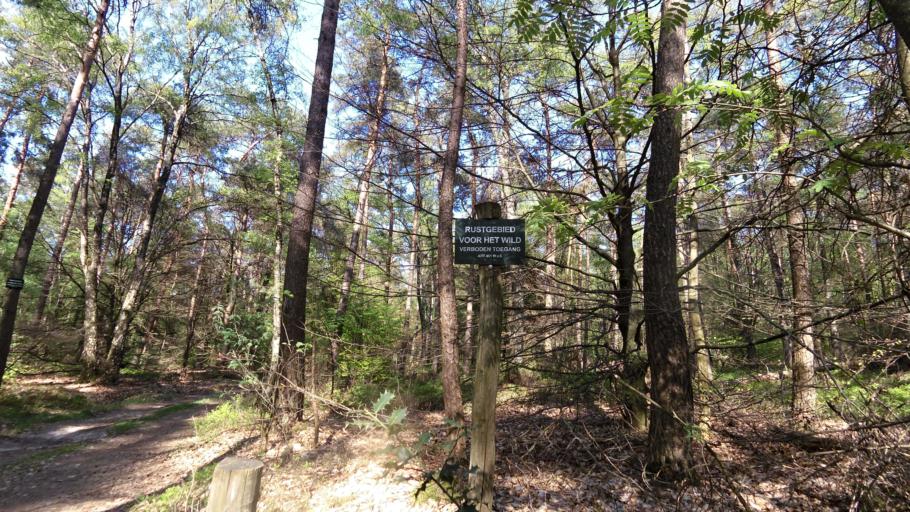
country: NL
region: Gelderland
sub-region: Gemeente Rozendaal
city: Rozendaal
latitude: 52.0197
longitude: 5.9617
